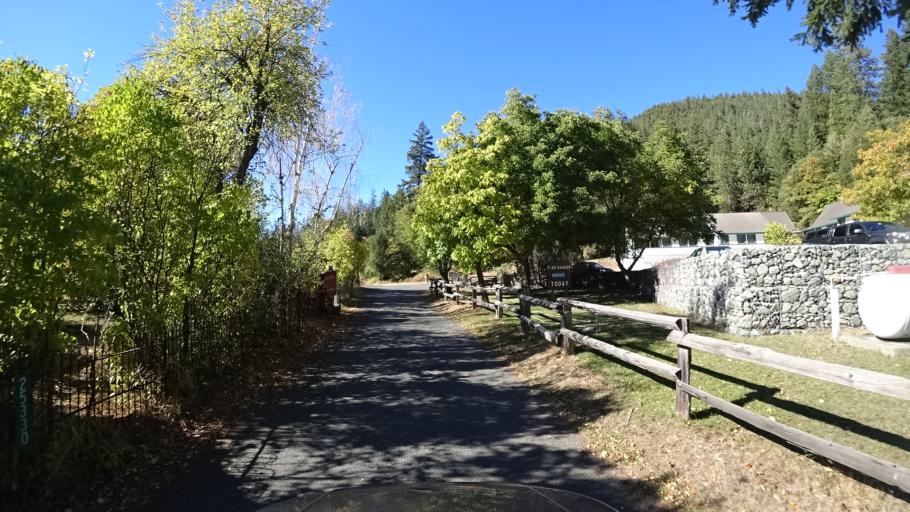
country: US
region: California
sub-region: Siskiyou County
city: Happy Camp
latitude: 41.2994
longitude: -123.1323
